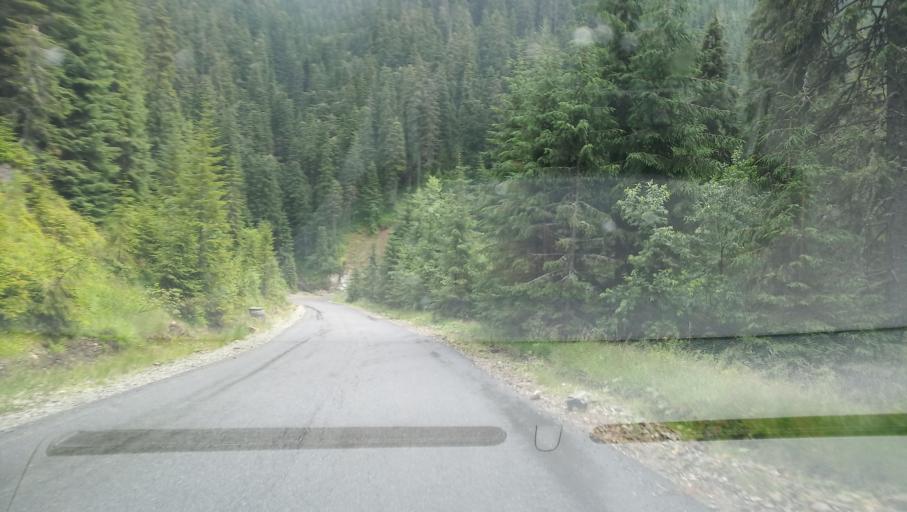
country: RO
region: Hunedoara
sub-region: Oras Petrila
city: Petrila
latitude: 45.4100
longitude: 23.5835
